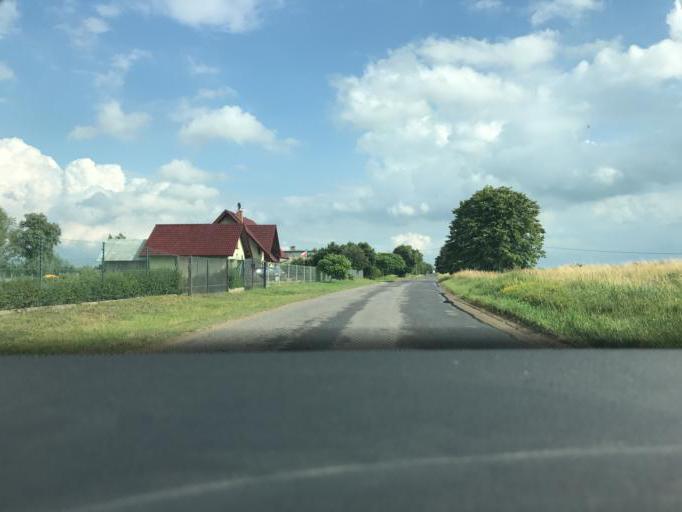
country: PL
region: Pomeranian Voivodeship
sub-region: Powiat gdanski
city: Cedry Wielkie
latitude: 54.3436
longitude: 18.7925
